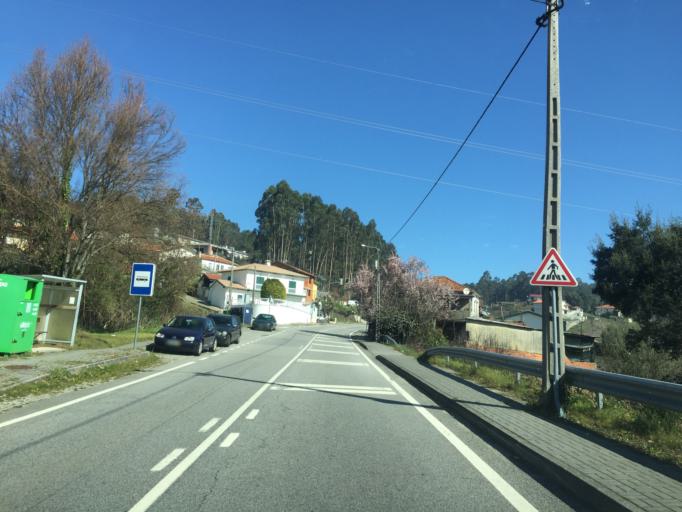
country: PT
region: Aveiro
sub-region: Vale de Cambra
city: Macieira de Cambra
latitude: 40.8874
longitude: -8.3608
